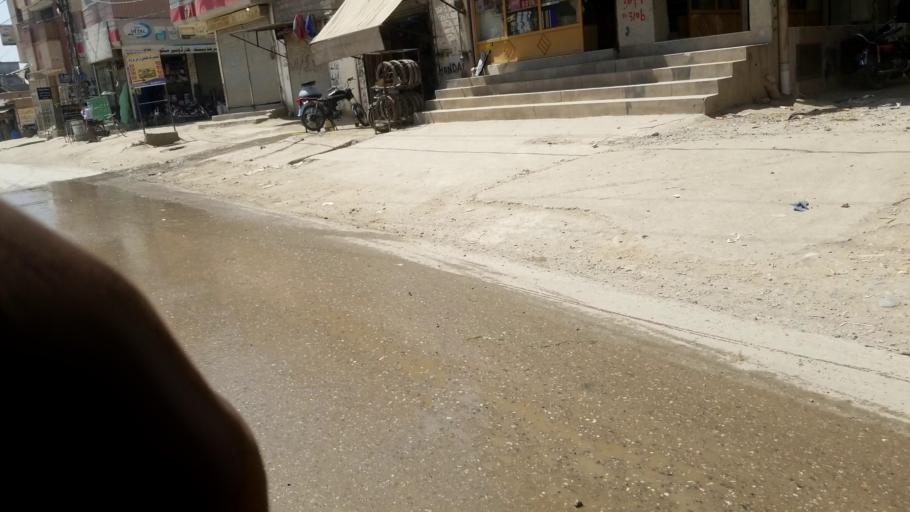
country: PK
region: Khyber Pakhtunkhwa
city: Peshawar
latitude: 34.0251
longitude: 71.4868
